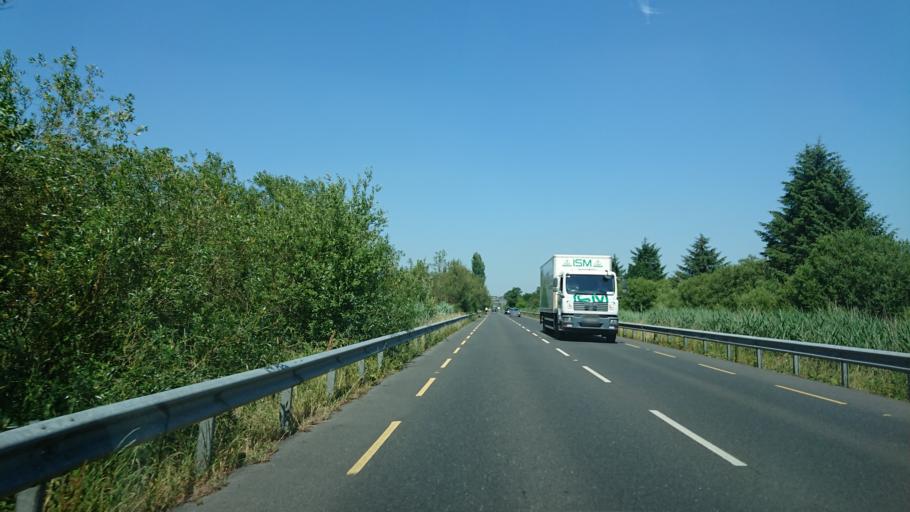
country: IE
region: Munster
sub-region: Waterford
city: Waterford
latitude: 52.2386
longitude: -7.1211
